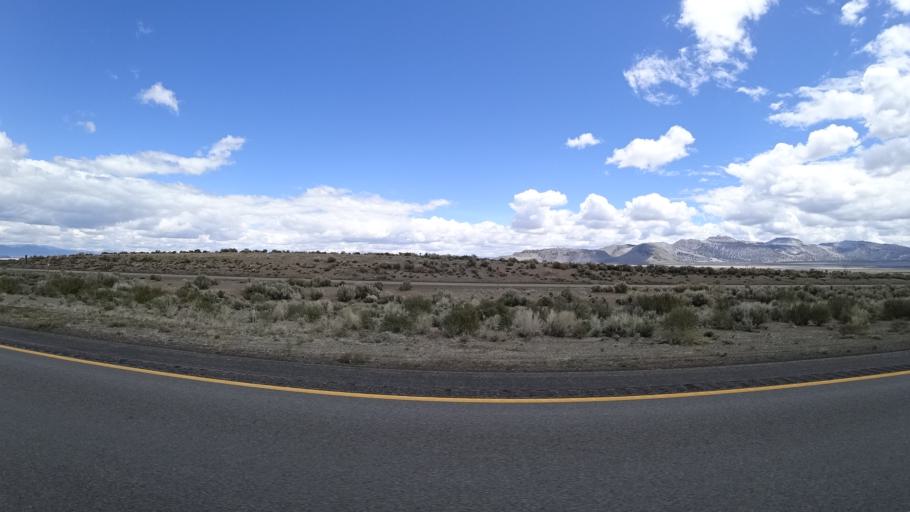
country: US
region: California
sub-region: Mono County
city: Mammoth Lakes
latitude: 37.9167
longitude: -119.0971
